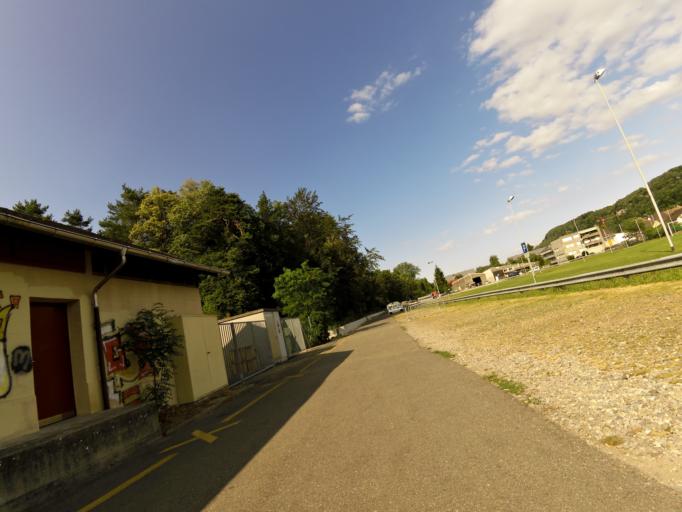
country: CH
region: Solothurn
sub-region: Bezirk Olten
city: Schonenwerd
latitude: 47.3795
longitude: 8.0026
